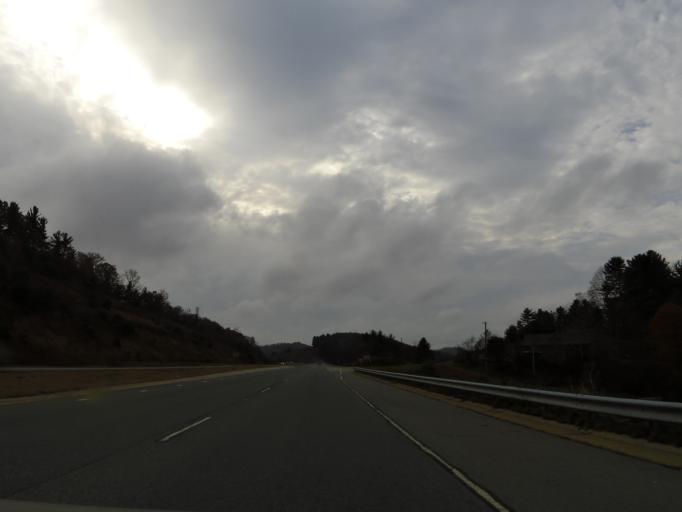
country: US
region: North Carolina
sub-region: Watauga County
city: Boone
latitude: 36.2352
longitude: -81.5656
